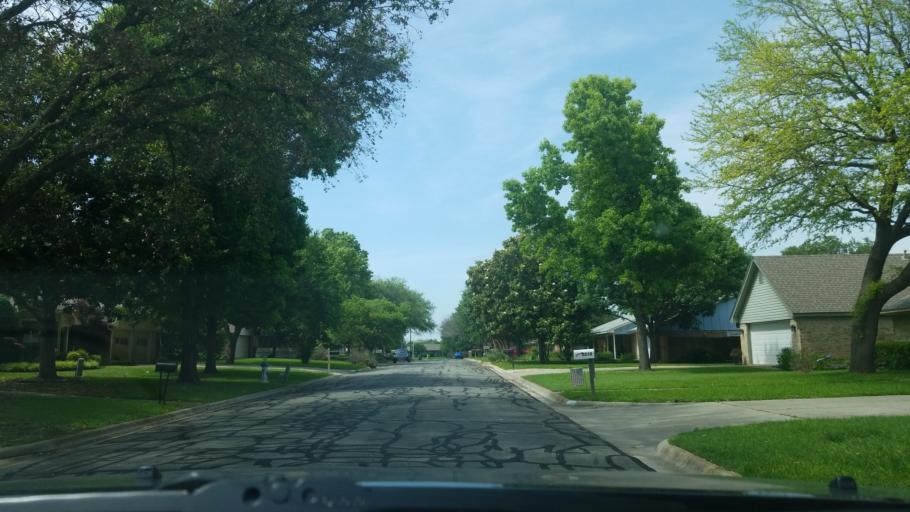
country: US
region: Texas
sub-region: Denton County
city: Denton
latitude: 33.2370
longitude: -97.1524
